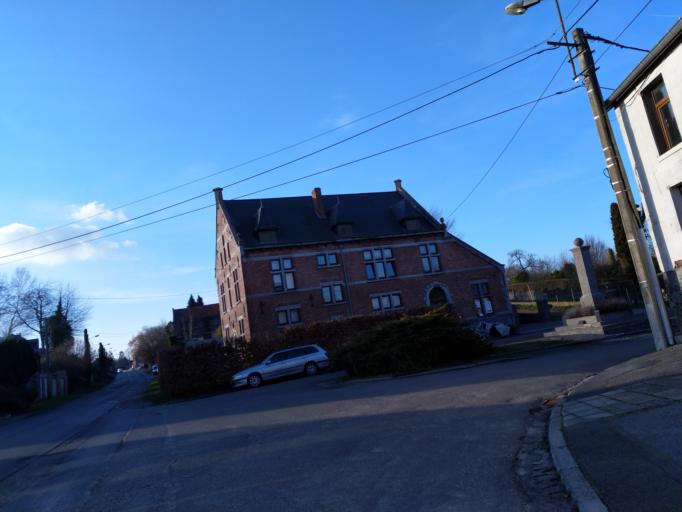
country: BE
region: Wallonia
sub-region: Province du Hainaut
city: Quevy-le-Petit
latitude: 50.3571
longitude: 3.8972
